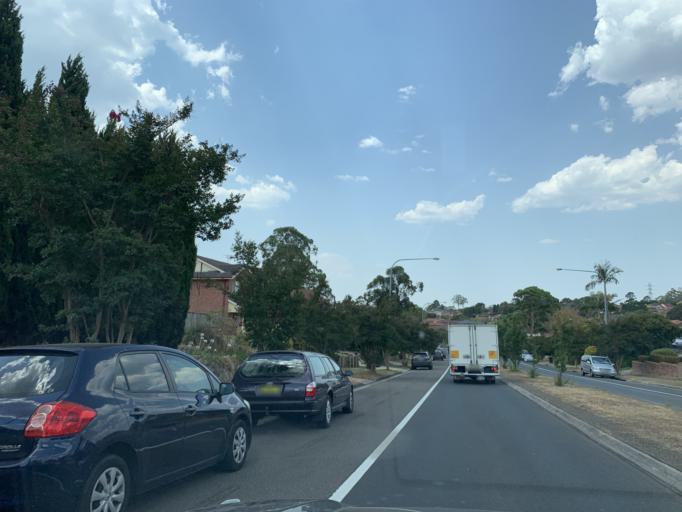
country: AU
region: New South Wales
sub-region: The Hills Shire
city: West Pennant
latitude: -33.7304
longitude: 151.0296
